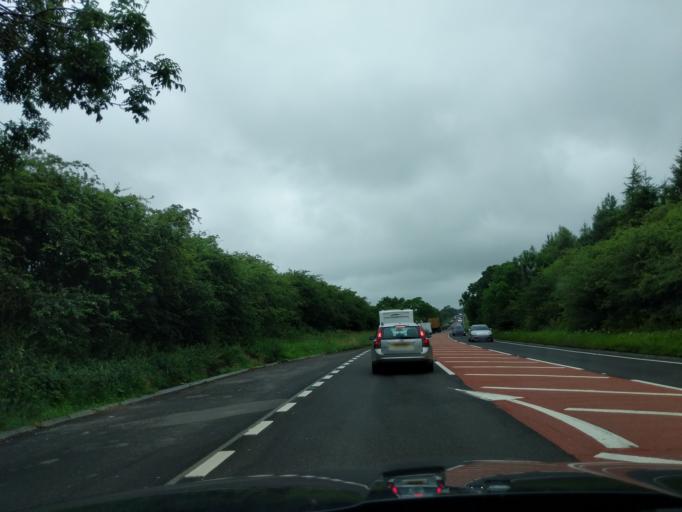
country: GB
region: England
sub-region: Northumberland
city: Felton
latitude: 55.2681
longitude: -1.7184
